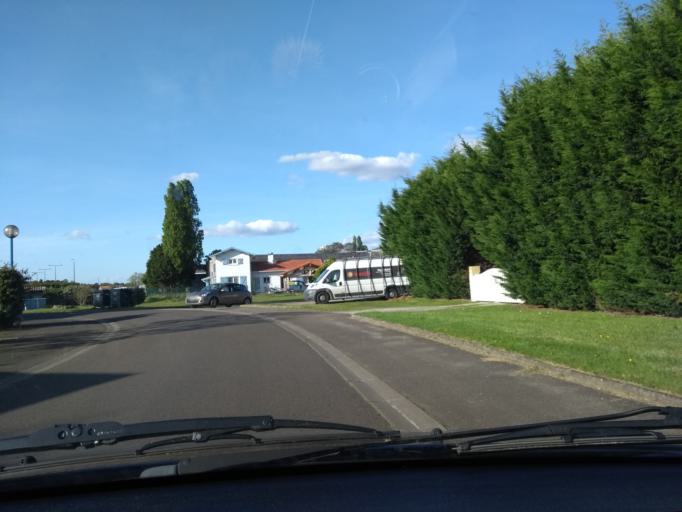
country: FR
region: Aquitaine
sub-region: Departement des Landes
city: Parentis-en-Born
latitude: 44.3547
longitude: -1.0713
